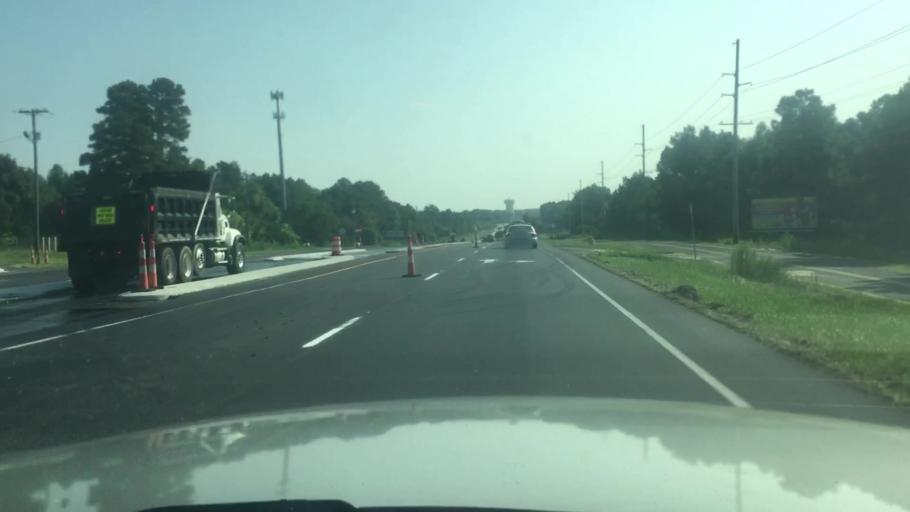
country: US
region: North Carolina
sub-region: Cumberland County
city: Fayetteville
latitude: 35.0260
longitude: -78.8877
